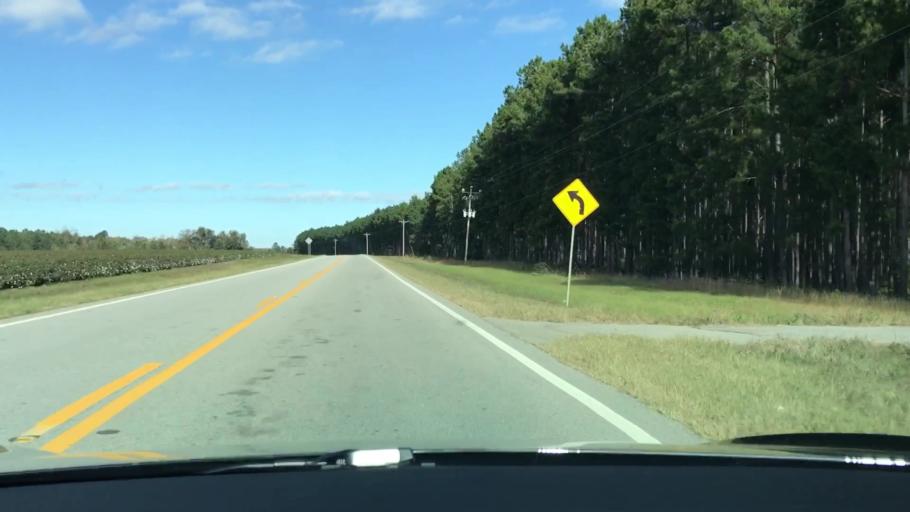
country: US
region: Georgia
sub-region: Glascock County
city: Gibson
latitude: 33.2828
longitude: -82.5050
